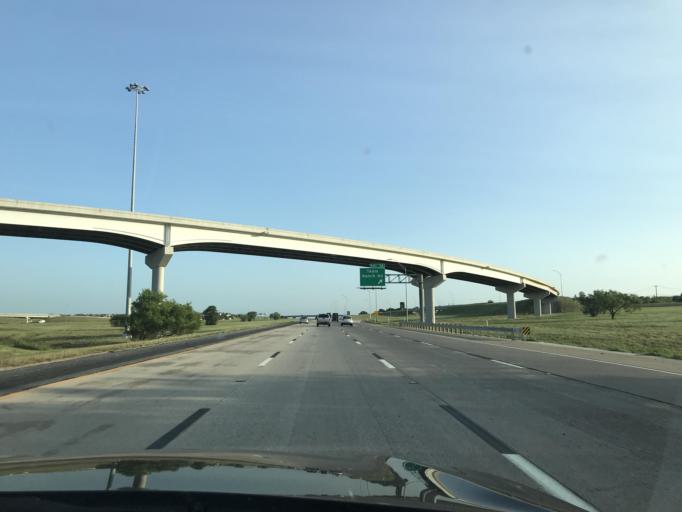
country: US
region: Texas
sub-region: Tarrant County
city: Benbrook
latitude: 32.6936
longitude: -97.4688
